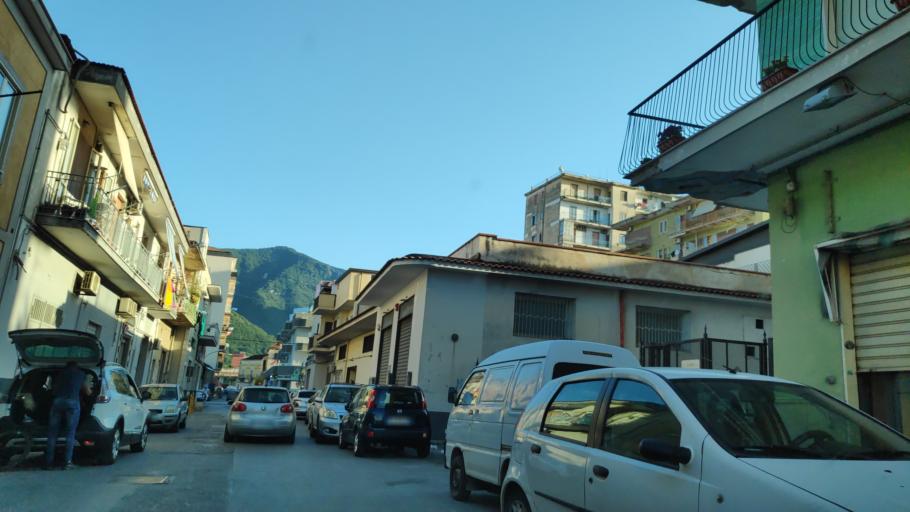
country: IT
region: Campania
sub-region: Provincia di Salerno
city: Pagani
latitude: 40.7491
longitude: 14.6148
